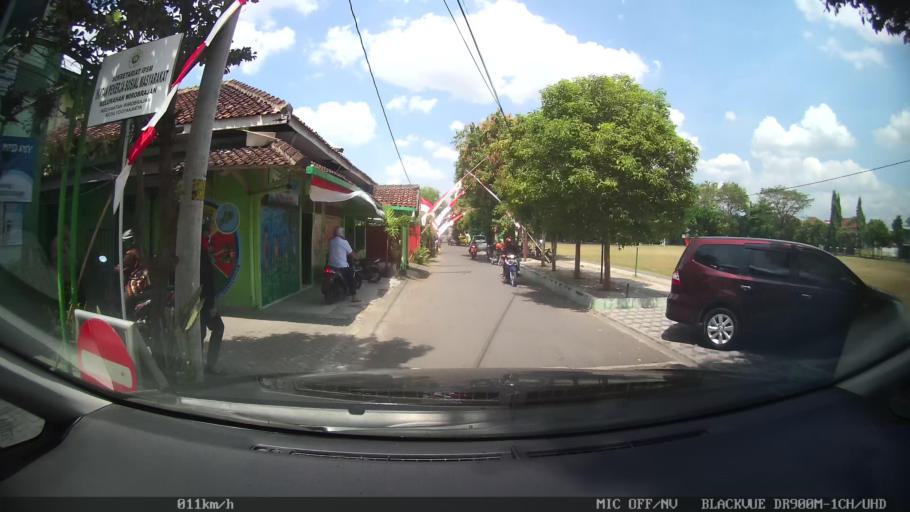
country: ID
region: Daerah Istimewa Yogyakarta
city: Yogyakarta
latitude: -7.8048
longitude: 110.3532
